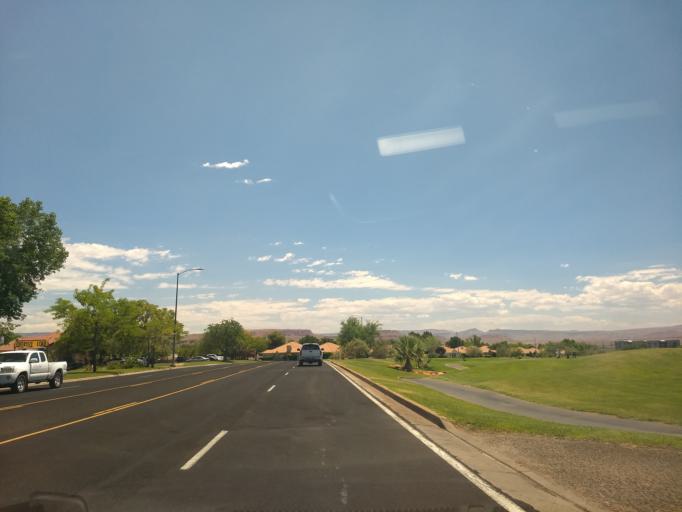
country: US
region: Utah
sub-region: Washington County
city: Washington
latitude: 37.1399
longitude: -113.5275
